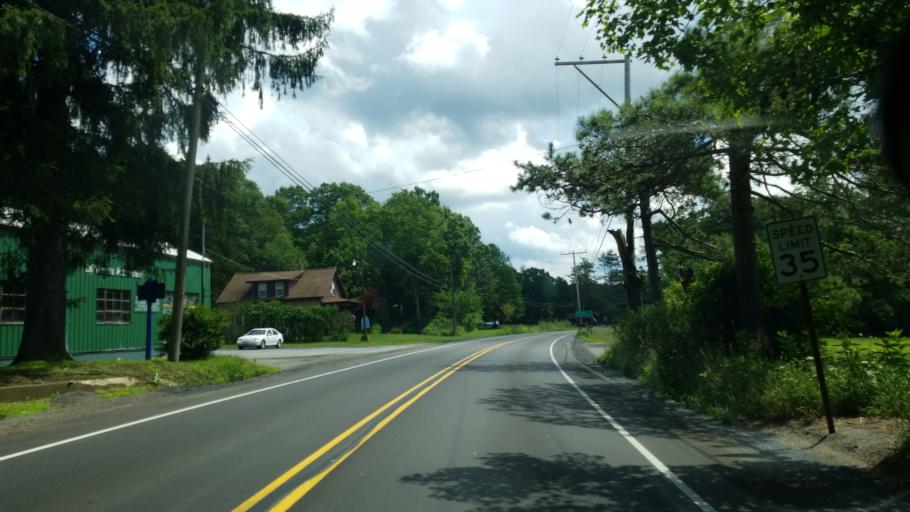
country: US
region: Pennsylvania
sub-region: Jefferson County
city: Brookville
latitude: 41.2712
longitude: -79.1093
